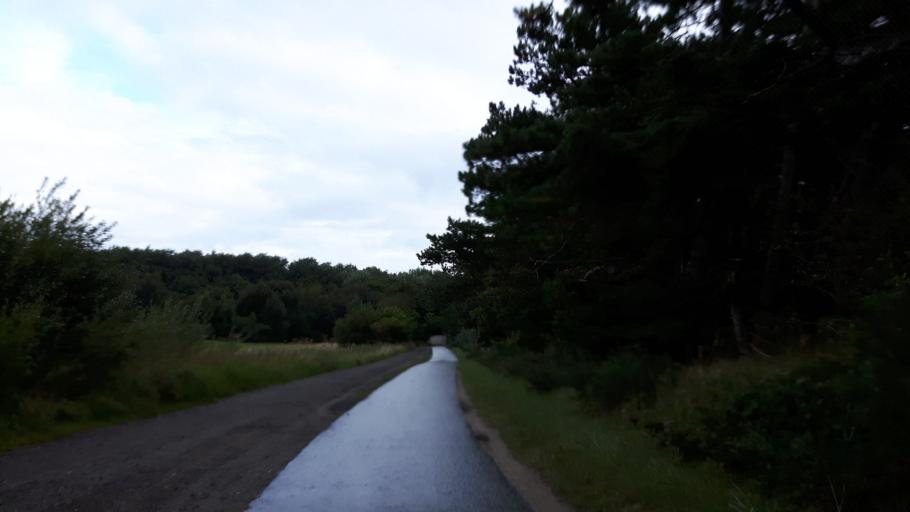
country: NL
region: Friesland
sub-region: Gemeente Ameland
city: Nes
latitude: 53.4515
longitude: 5.7570
